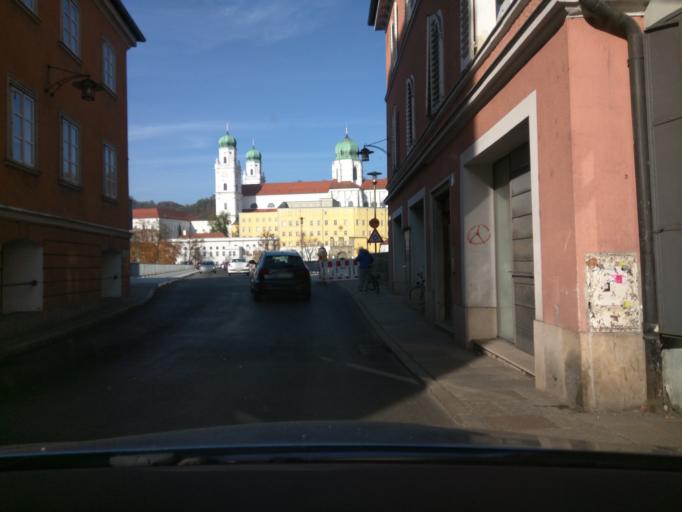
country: DE
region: Bavaria
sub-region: Lower Bavaria
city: Passau
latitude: 48.5713
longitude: 13.4661
